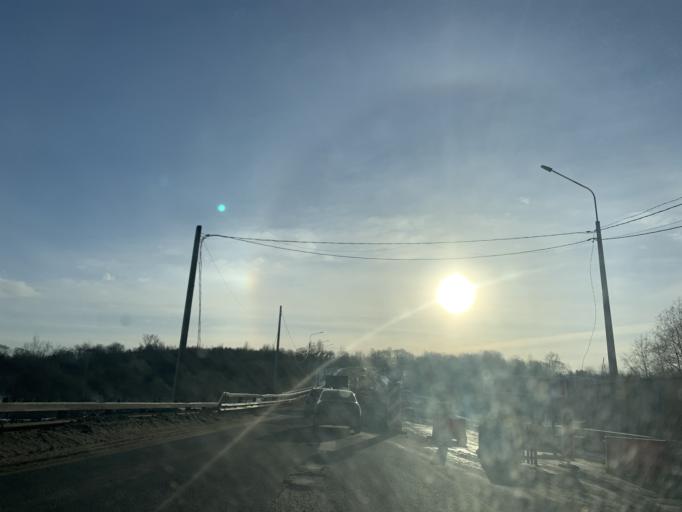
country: RU
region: Jaroslavl
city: Konstantinovskiy
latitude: 57.8089
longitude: 39.5789
